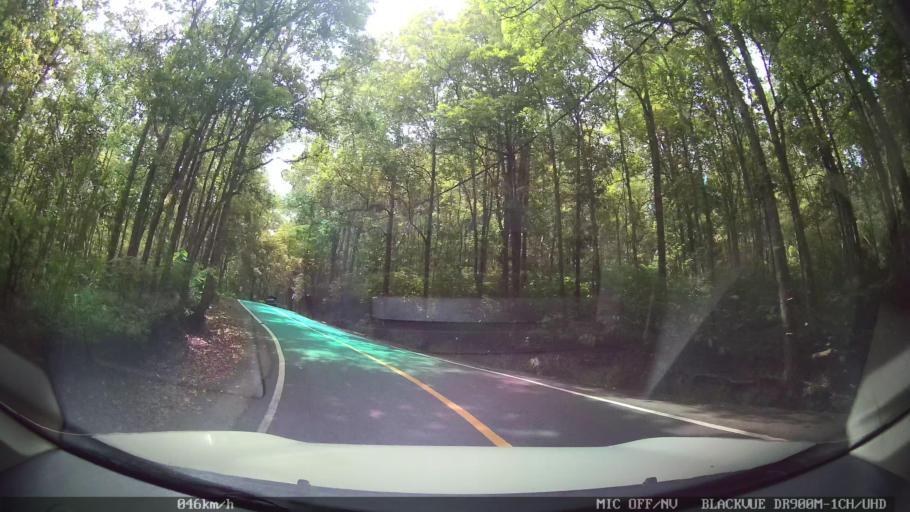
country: ID
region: Bali
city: Banjar Buahan
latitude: -8.2945
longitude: 115.3912
